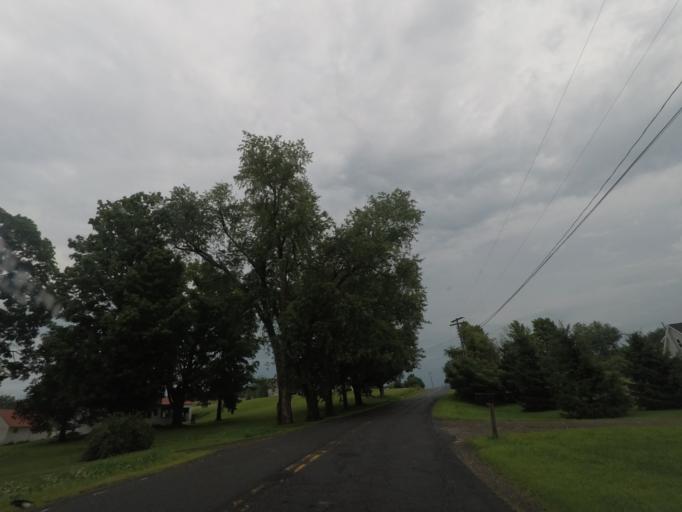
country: US
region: New York
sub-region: Rensselaer County
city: Poestenkill
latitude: 42.8043
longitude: -73.5633
